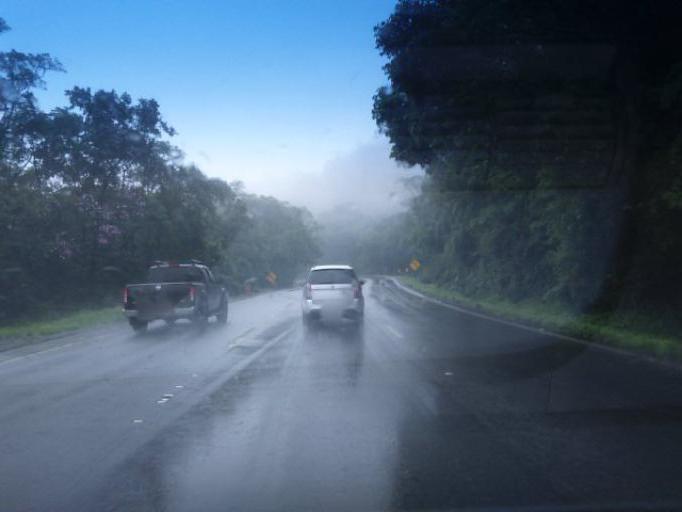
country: BR
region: Parana
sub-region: Guaratuba
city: Guaratuba
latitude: -25.8536
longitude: -48.9525
